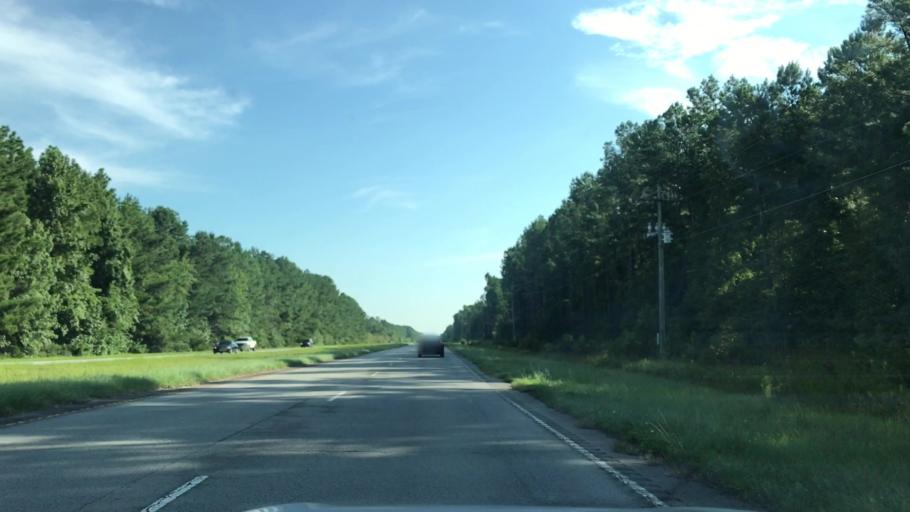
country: US
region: South Carolina
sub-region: Charleston County
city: Awendaw
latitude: 33.0038
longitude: -79.6425
